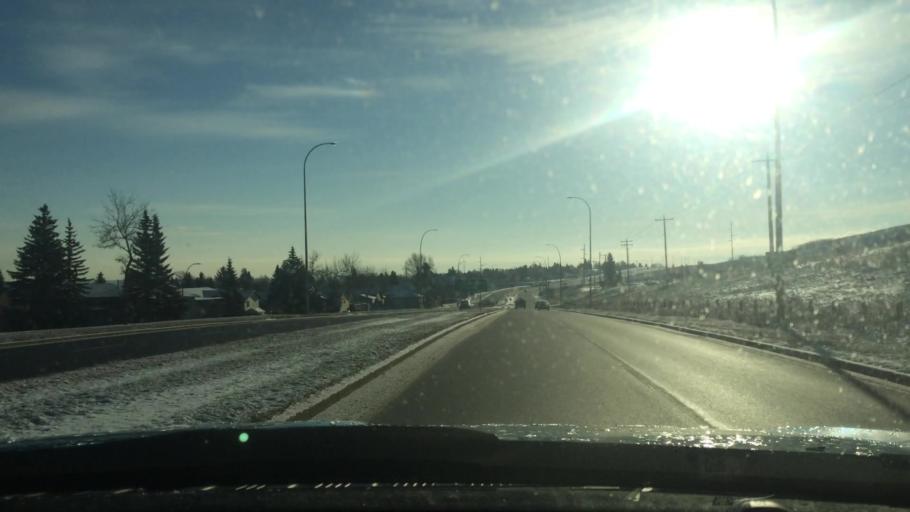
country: CA
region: Alberta
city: Calgary
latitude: 51.1271
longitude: -114.1019
